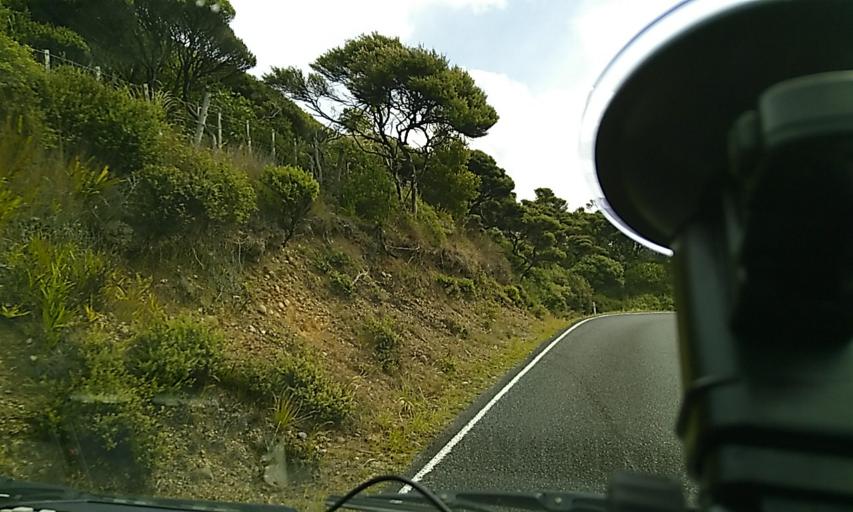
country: NZ
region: Northland
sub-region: Far North District
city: Ahipara
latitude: -35.5385
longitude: 173.3746
